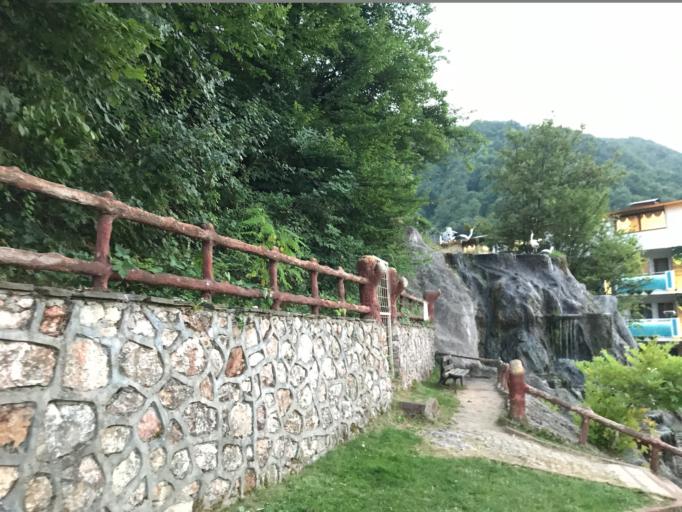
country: TR
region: Bursa
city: Tahtakopru
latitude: 39.9273
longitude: 29.5862
